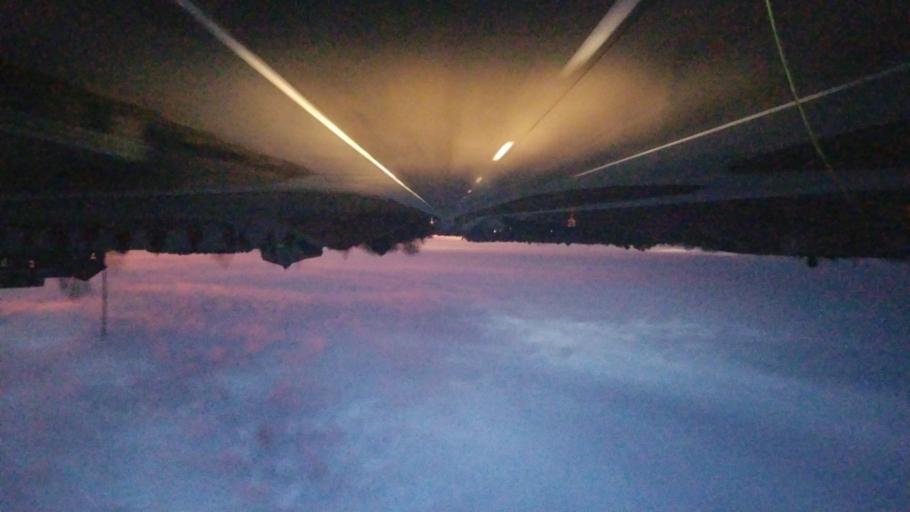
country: US
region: Missouri
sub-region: Shannon County
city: Winona
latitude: 36.9948
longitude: -91.5115
